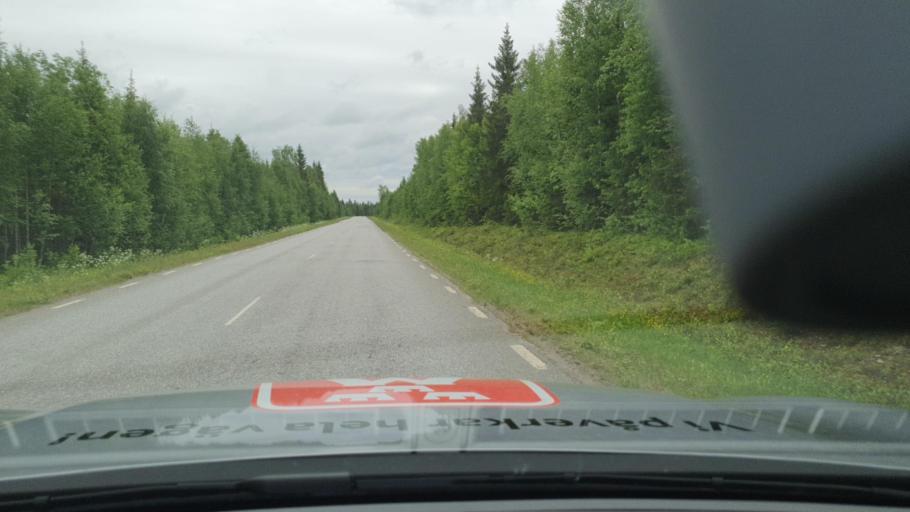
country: SE
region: Norrbotten
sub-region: Lulea Kommun
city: Ranea
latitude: 65.8693
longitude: 22.2267
